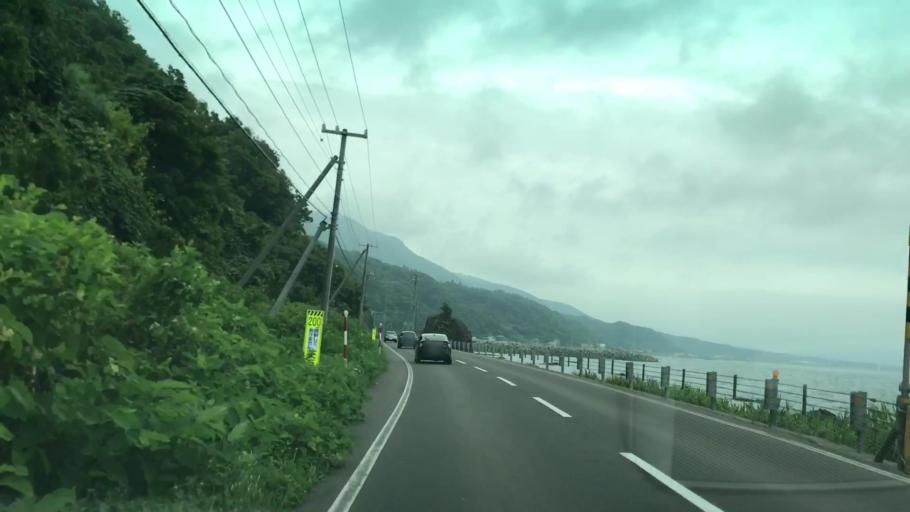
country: JP
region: Hokkaido
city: Iwanai
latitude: 42.8013
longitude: 140.3073
